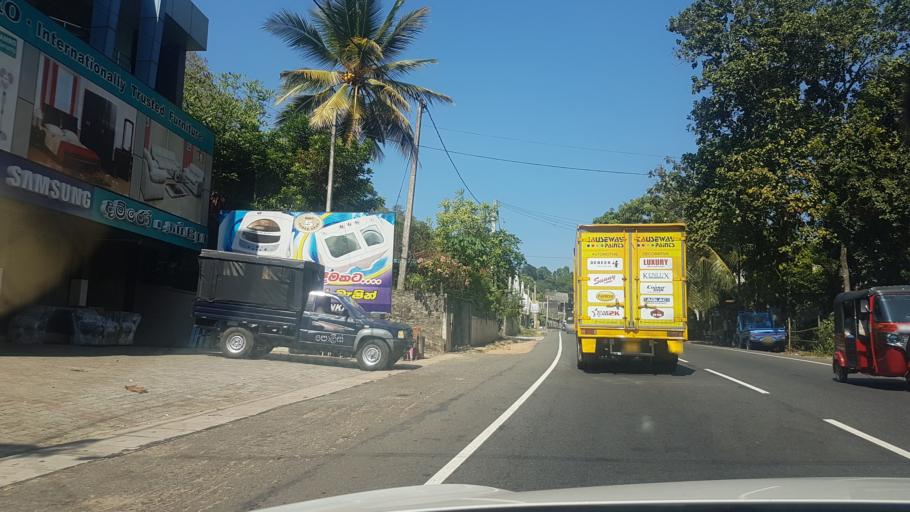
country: LK
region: North Western
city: Kurunegala
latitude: 7.3332
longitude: 80.2983
